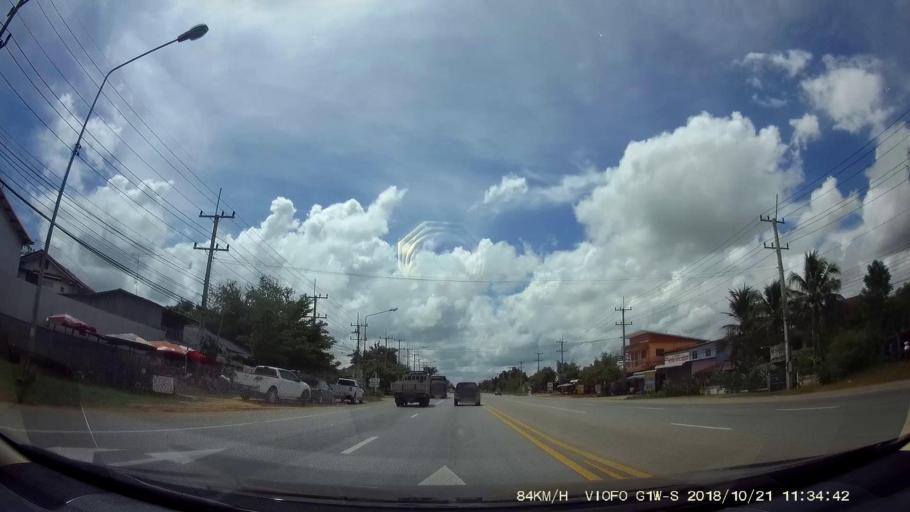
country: TH
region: Chaiyaphum
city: Chaiyaphum
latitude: 15.7294
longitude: 102.0217
